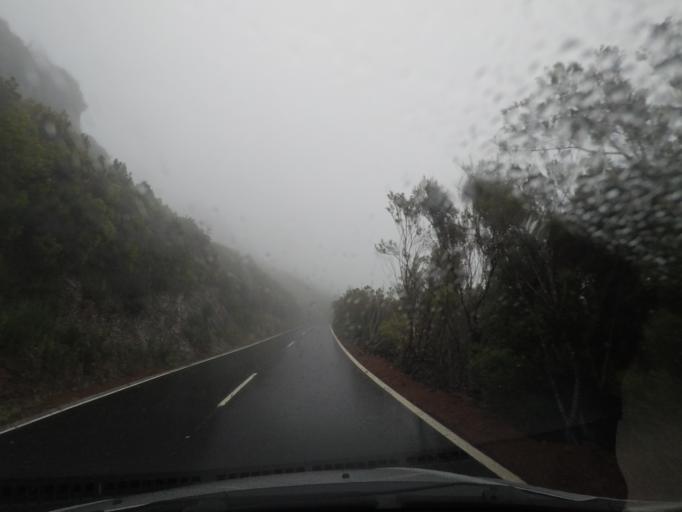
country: PT
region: Madeira
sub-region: Santana
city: Santana
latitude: 32.7683
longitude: -16.9196
